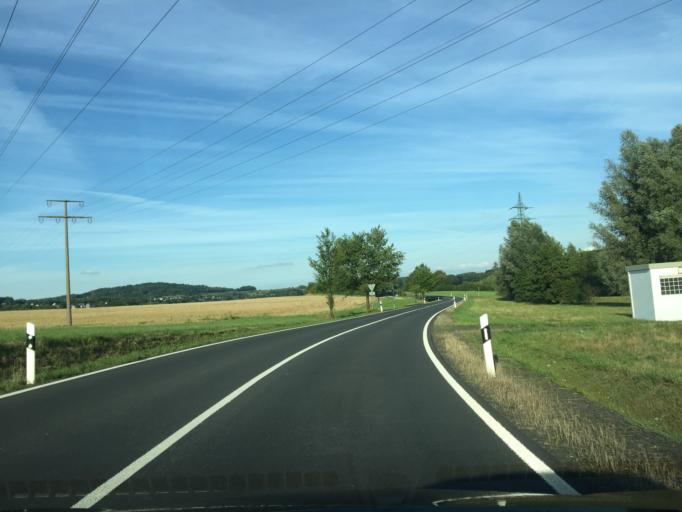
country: DE
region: Rheinland-Pfalz
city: Heiligenroth
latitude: 50.4540
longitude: 7.8573
